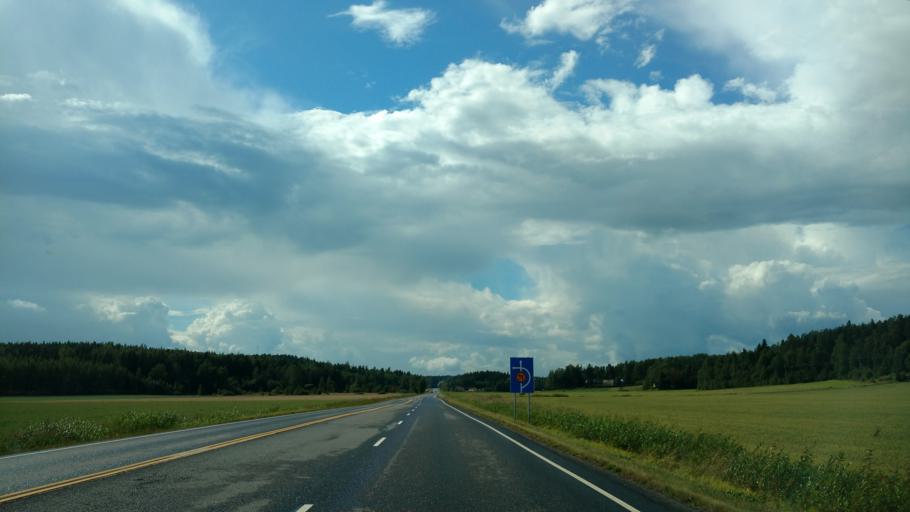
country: FI
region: Varsinais-Suomi
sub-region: Salo
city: Halikko
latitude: 60.3764
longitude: 22.9616
